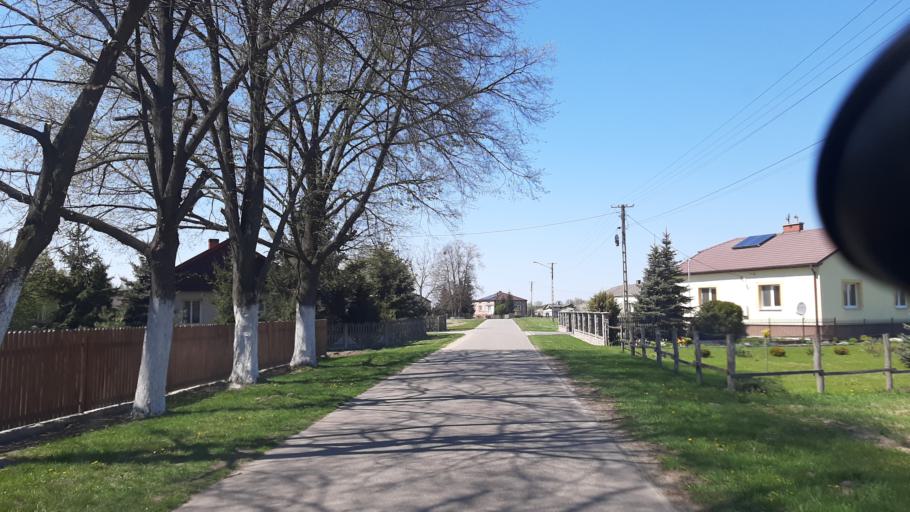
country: PL
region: Lublin Voivodeship
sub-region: Powiat lubelski
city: Garbow
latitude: 51.4021
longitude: 22.3273
